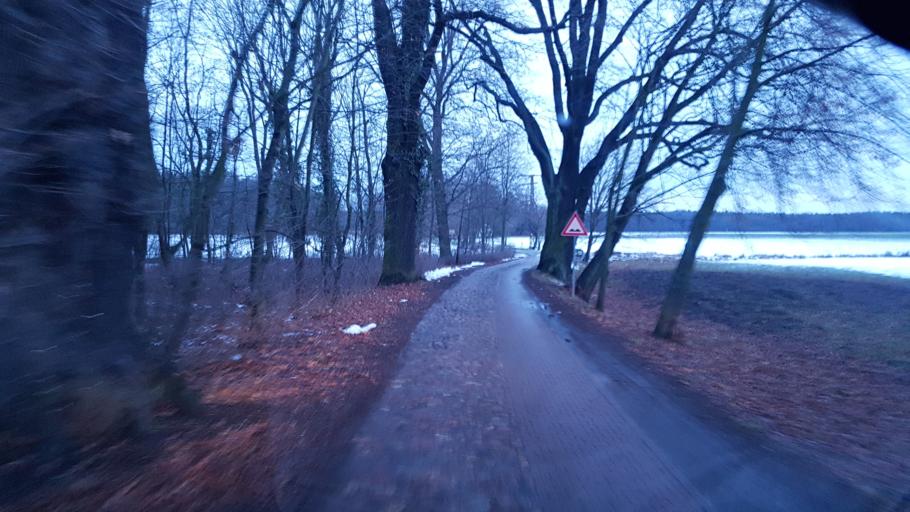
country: DE
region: Brandenburg
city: Neupetershain
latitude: 51.6071
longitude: 14.1277
